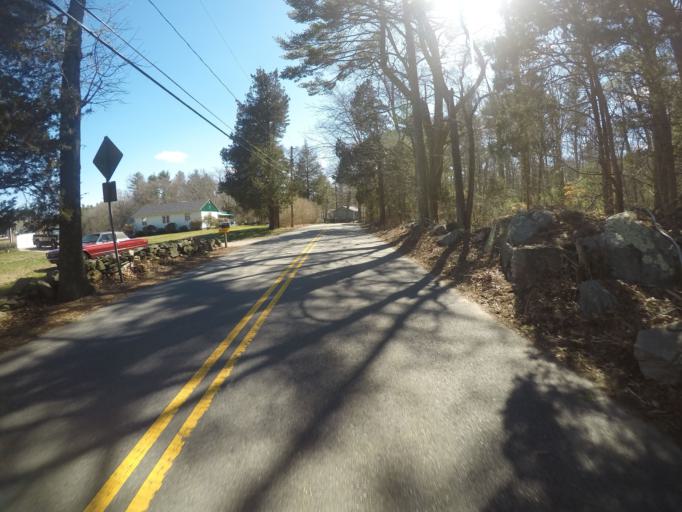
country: US
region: Massachusetts
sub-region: Bristol County
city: Easton
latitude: 42.0035
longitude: -71.0963
